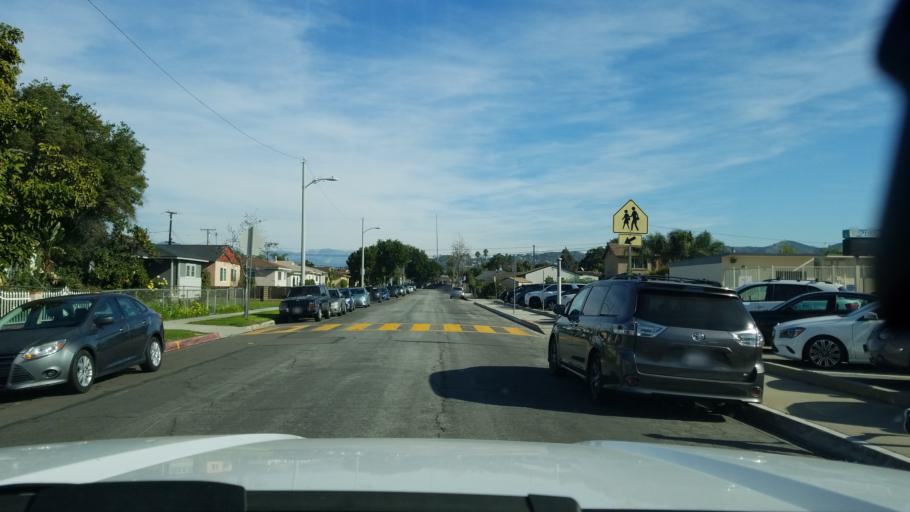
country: US
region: California
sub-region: Los Angeles County
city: West Whittier-Los Nietos
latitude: 33.9804
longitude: -118.0721
